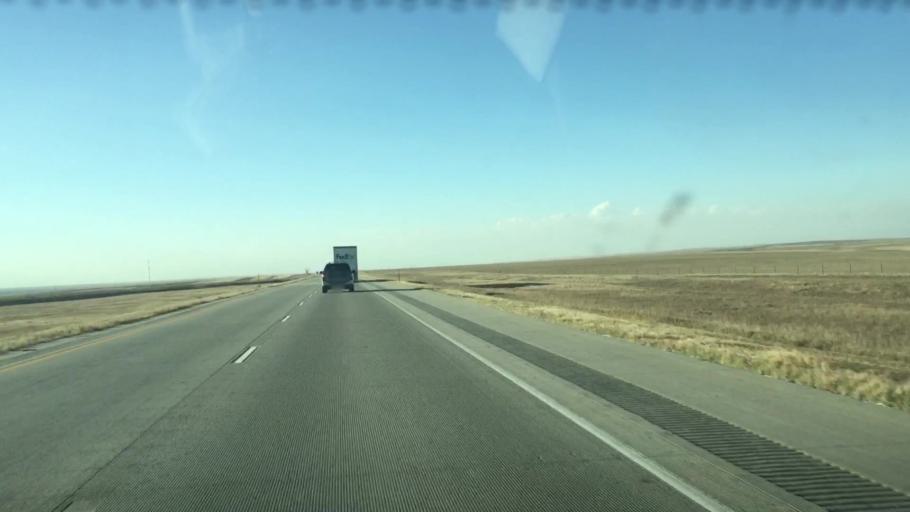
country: US
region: Colorado
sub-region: Lincoln County
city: Limon
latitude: 39.4181
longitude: -103.9061
